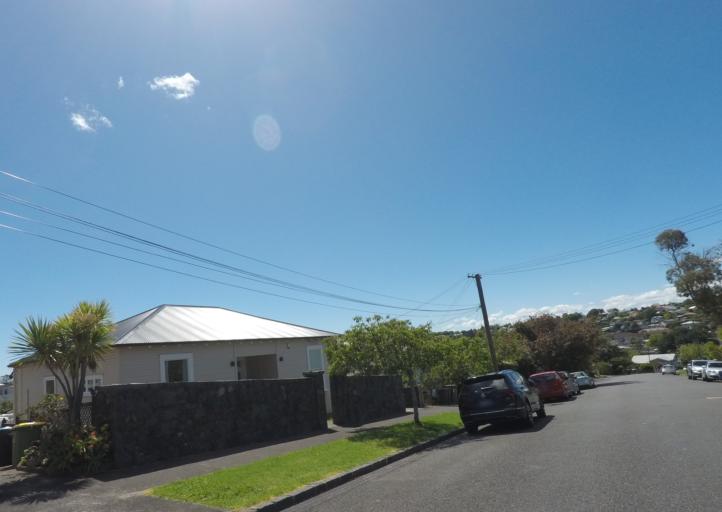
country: NZ
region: Auckland
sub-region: Auckland
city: Auckland
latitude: -36.8704
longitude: 174.7336
